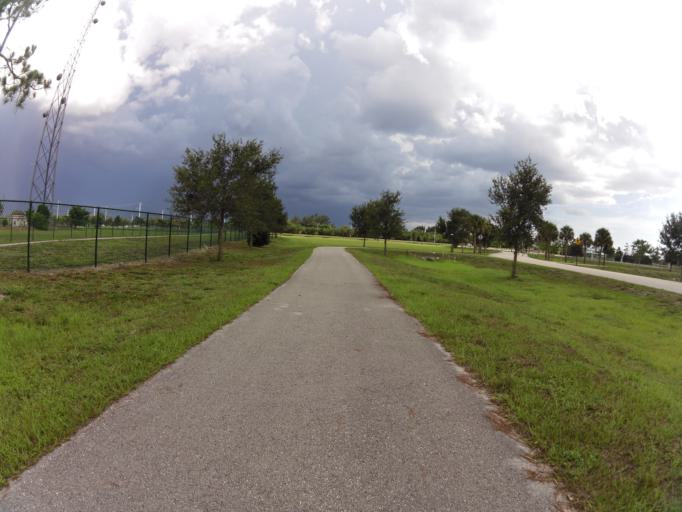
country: US
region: Florida
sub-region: Broward County
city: Southwest Ranches
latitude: 26.0660
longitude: -80.3395
